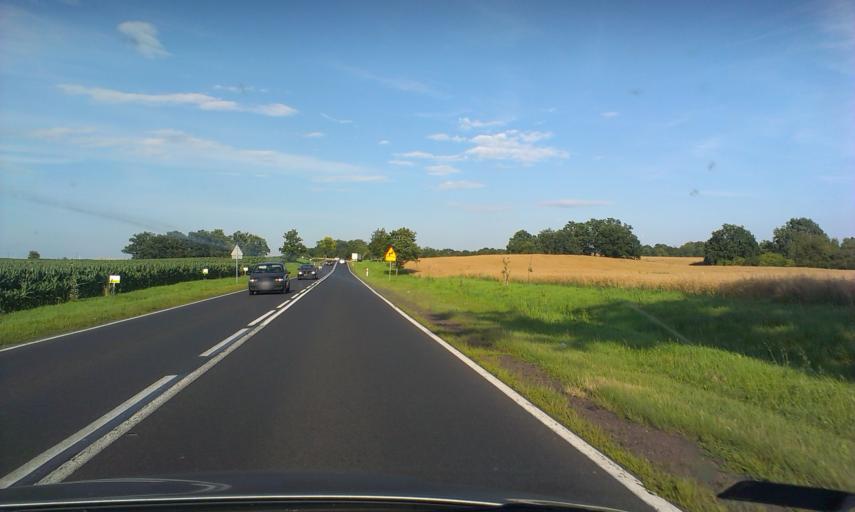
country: PL
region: Kujawsko-Pomorskie
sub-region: Powiat bydgoski
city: Sicienko
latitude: 53.1675
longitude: 17.7604
